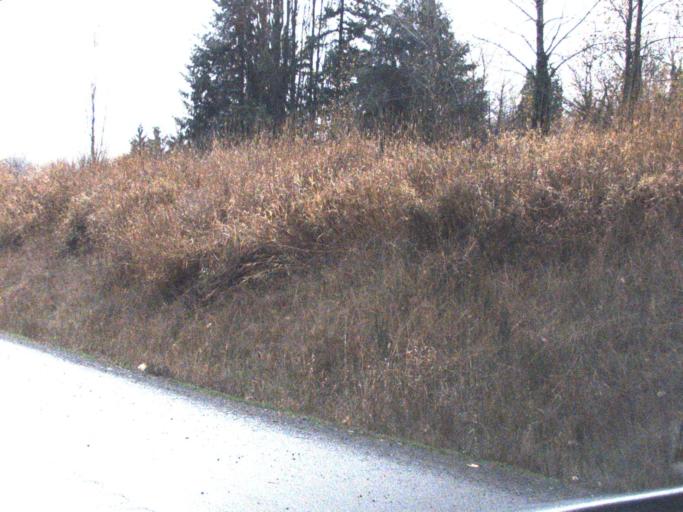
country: US
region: Washington
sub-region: Snohomish County
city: Snohomish
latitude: 47.9341
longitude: -122.0709
